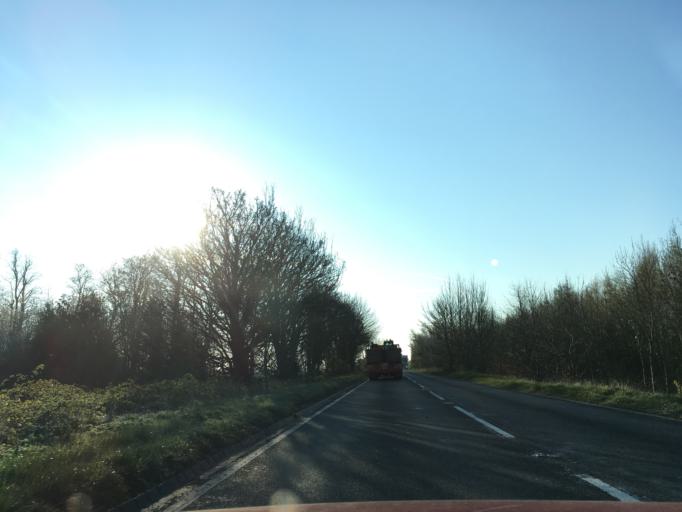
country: GB
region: England
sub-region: Oxfordshire
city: Burford
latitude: 51.8099
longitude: -1.6697
